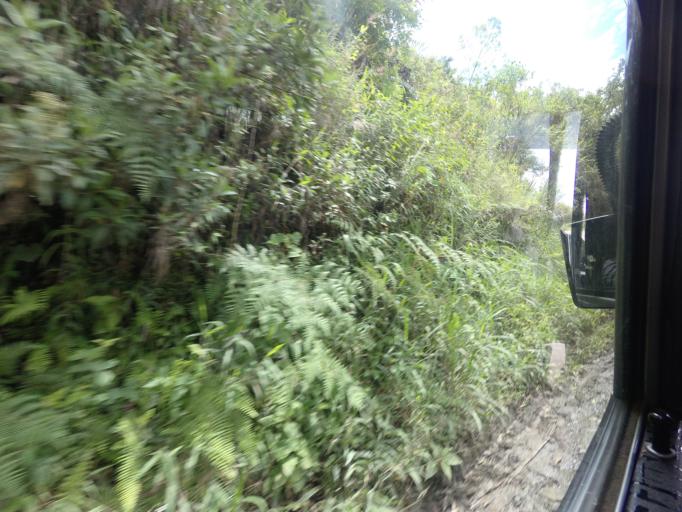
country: CO
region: Huila
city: Isnos
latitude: 1.9459
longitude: -76.2761
